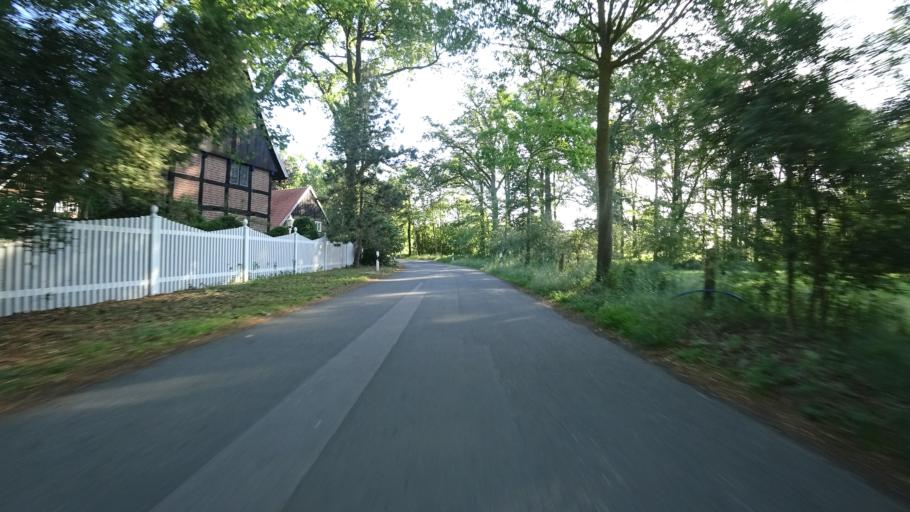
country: DE
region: North Rhine-Westphalia
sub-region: Regierungsbezirk Detmold
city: Rheda-Wiedenbruck
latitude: 51.8678
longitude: 8.3146
